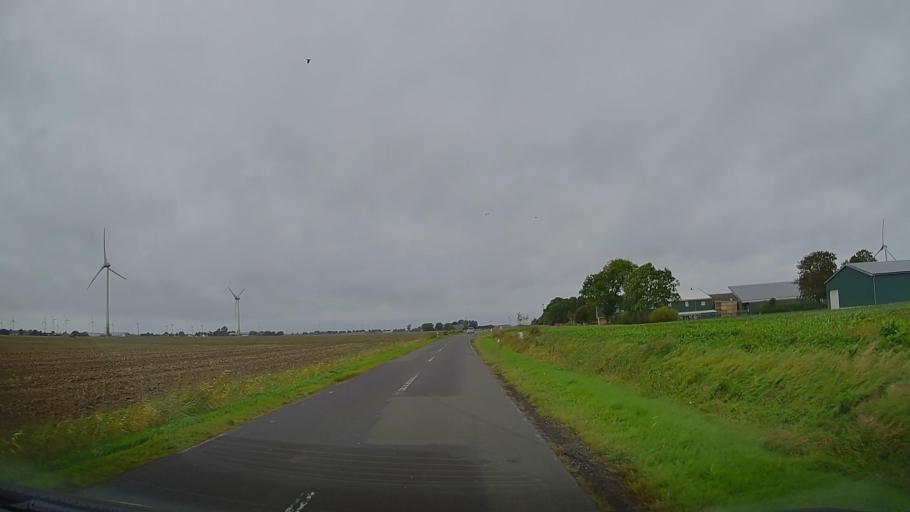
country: DE
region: Schleswig-Holstein
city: Marnerdeich
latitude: 53.9216
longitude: 8.9885
